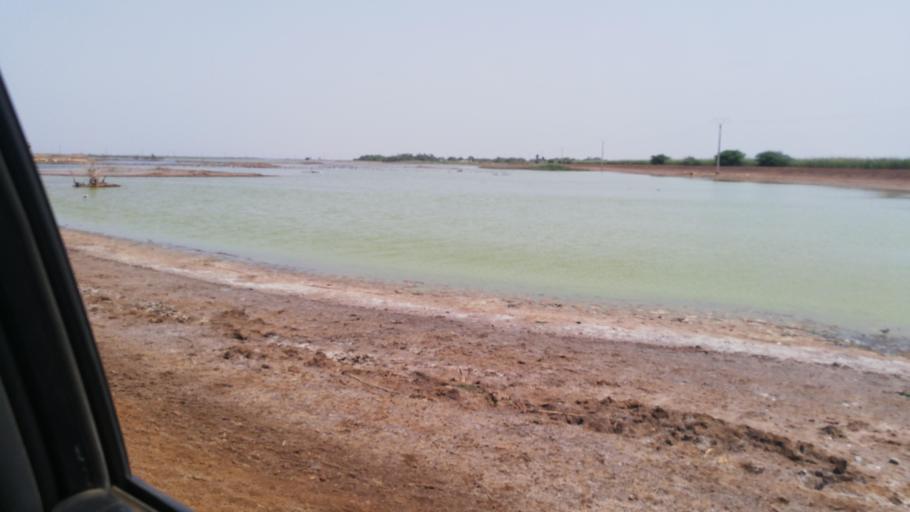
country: SN
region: Saint-Louis
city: Saint-Louis
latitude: 16.3616
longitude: -16.2766
